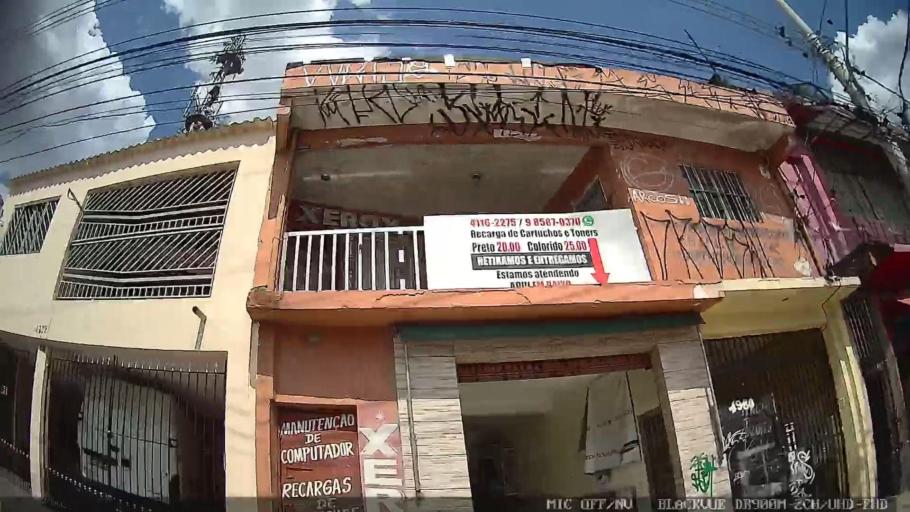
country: BR
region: Sao Paulo
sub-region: Sao Caetano Do Sul
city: Sao Caetano do Sul
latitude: -23.5529
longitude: -46.4794
